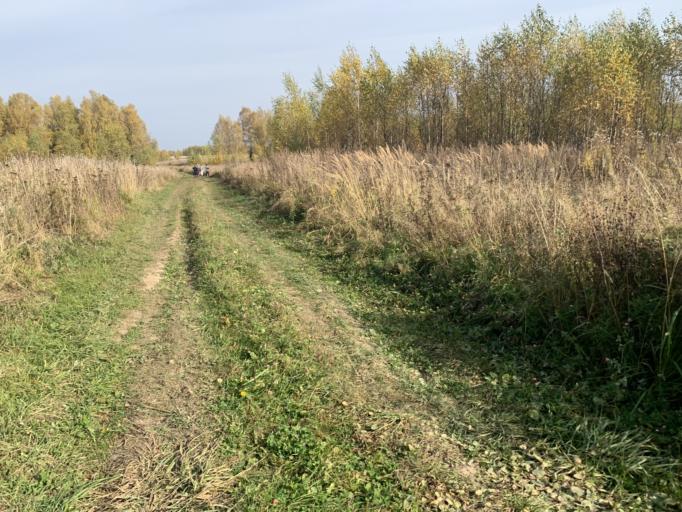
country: RU
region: Jaroslavl
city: Porech'ye-Rybnoye
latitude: 57.0019
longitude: 39.3965
